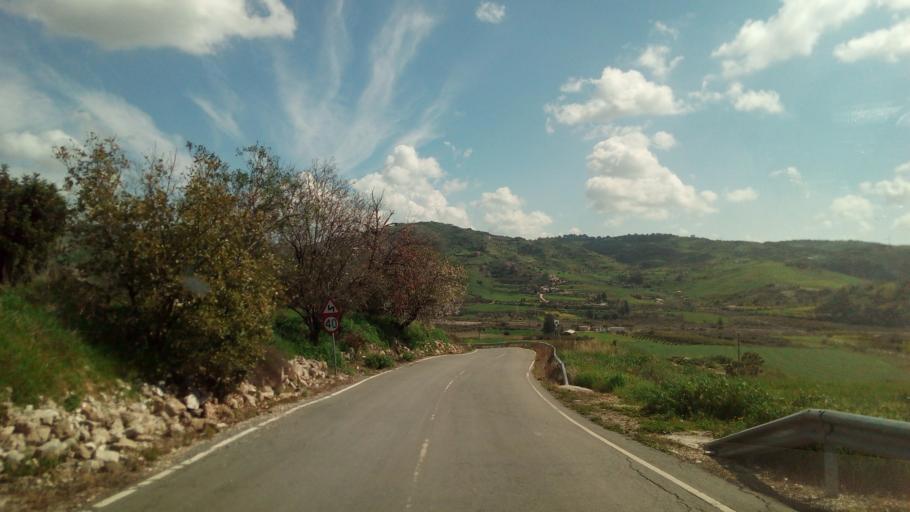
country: CY
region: Pafos
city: Mesogi
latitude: 34.7753
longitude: 32.5720
